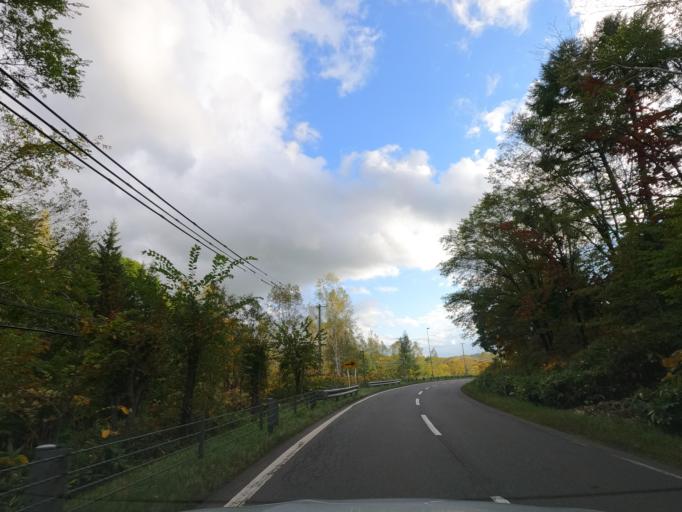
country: JP
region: Hokkaido
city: Date
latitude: 42.6552
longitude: 141.0682
